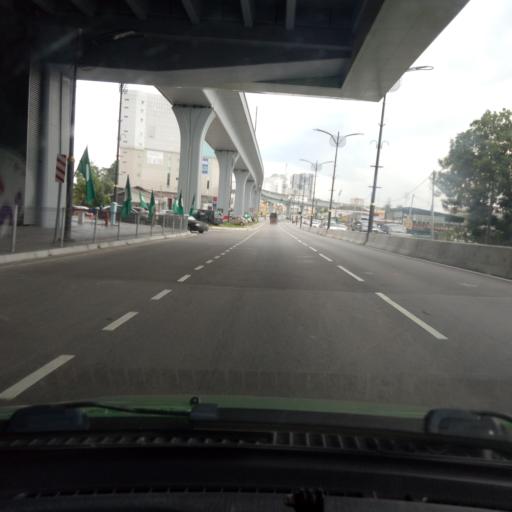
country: MY
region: Selangor
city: Kampong Baharu Balakong
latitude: 3.0005
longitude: 101.7842
